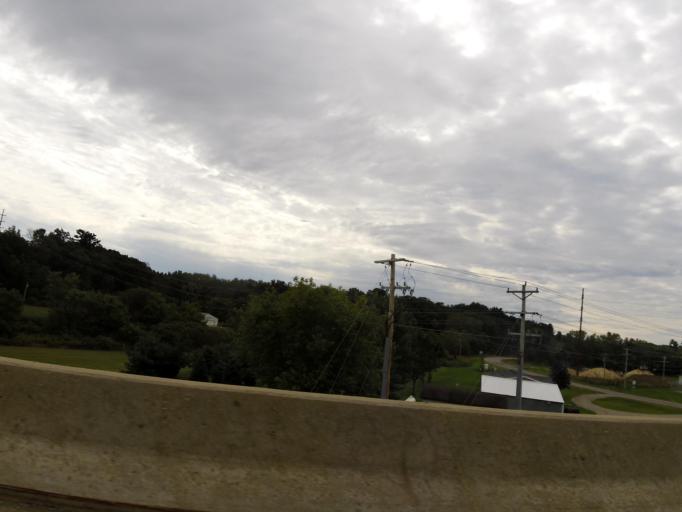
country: US
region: Wisconsin
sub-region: Monroe County
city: Tomah
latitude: 43.9439
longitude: -90.5775
